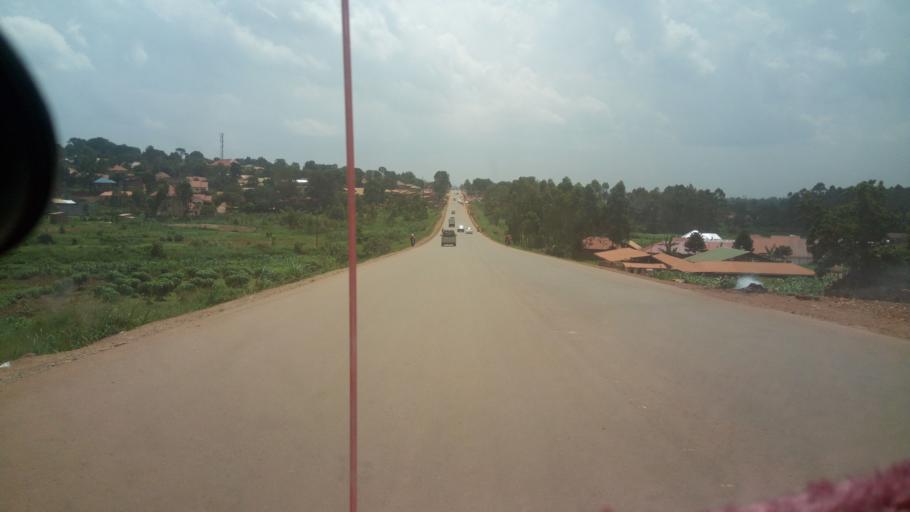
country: UG
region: Central Region
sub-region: Wakiso District
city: Wakiso
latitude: 0.3866
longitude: 32.5140
